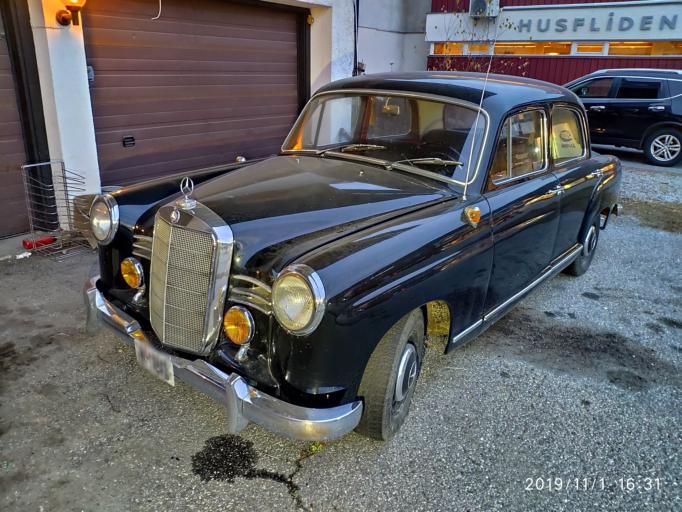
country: NO
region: Buskerud
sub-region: Gol
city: Gol
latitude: 60.7019
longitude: 8.9383
